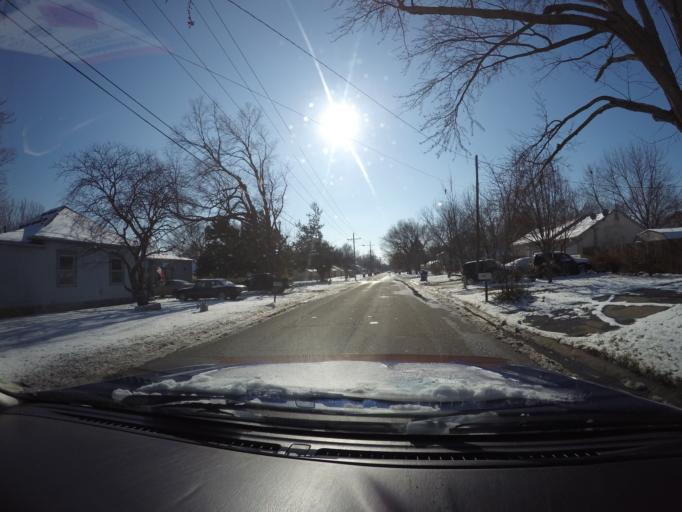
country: US
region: Kansas
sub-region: Johnson County
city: Olathe
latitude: 38.8885
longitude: -94.8254
